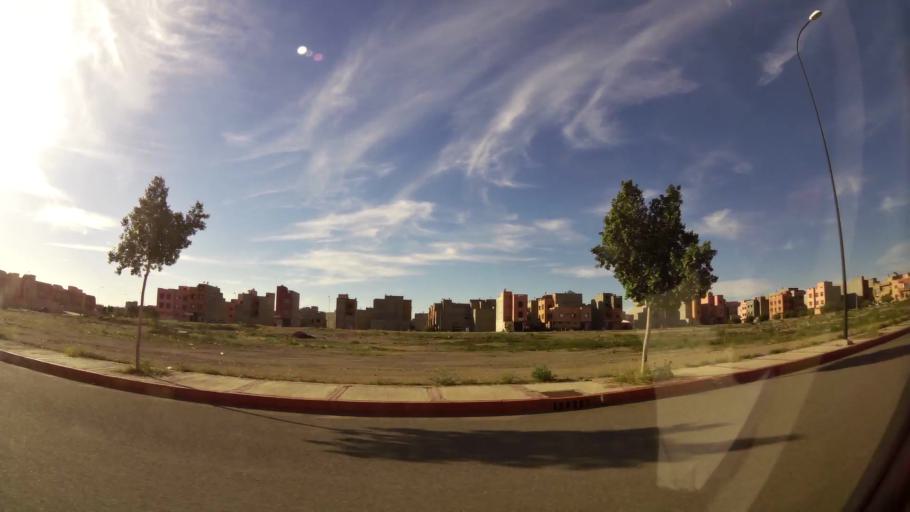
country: MA
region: Marrakech-Tensift-Al Haouz
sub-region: Marrakech
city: Marrakesh
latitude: 31.7500
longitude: -8.1032
